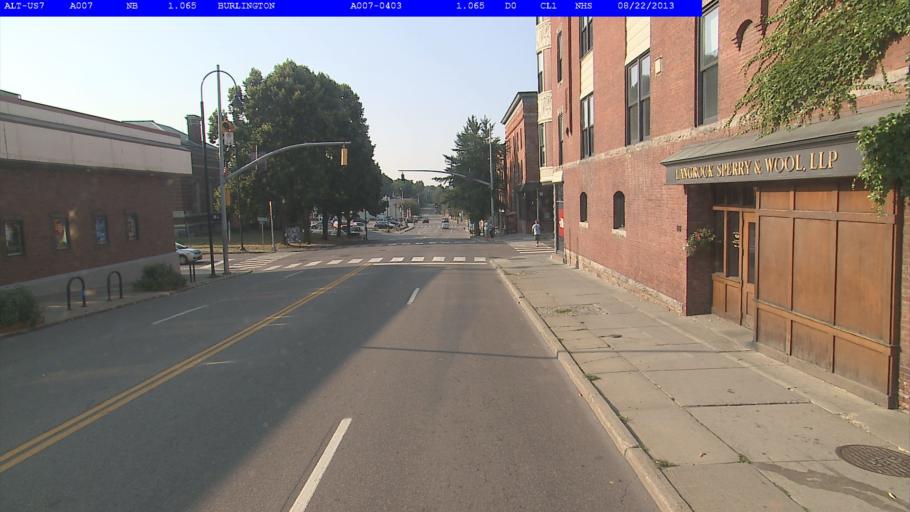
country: US
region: Vermont
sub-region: Chittenden County
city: Burlington
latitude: 44.4775
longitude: -73.2111
